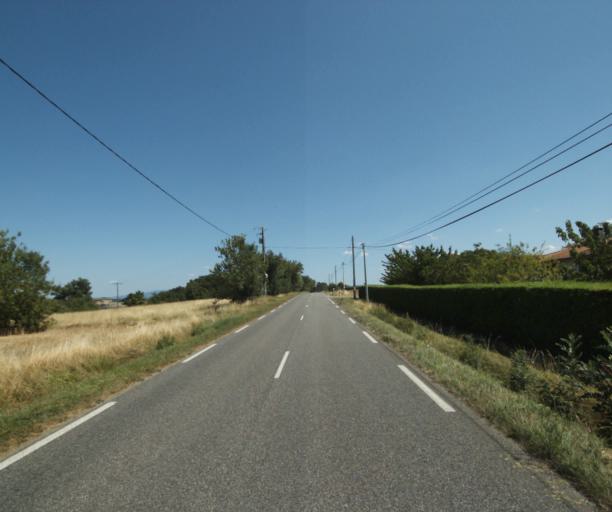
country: FR
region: Midi-Pyrenees
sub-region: Departement de la Haute-Garonne
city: Saint-Felix-Lauragais
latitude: 43.5008
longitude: 1.8807
